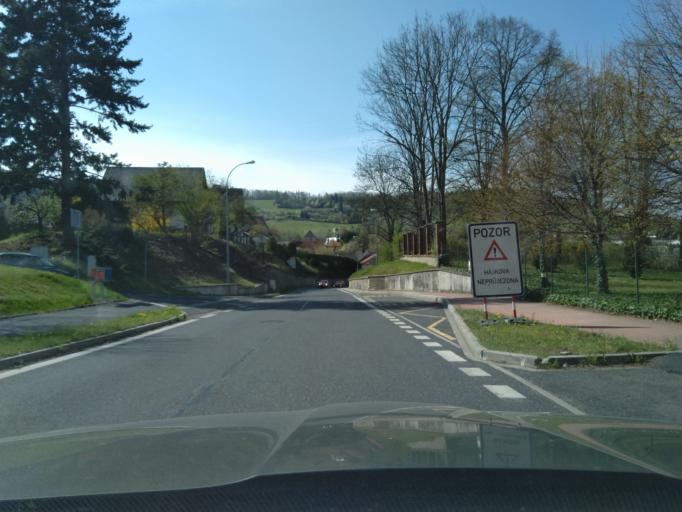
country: CZ
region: Plzensky
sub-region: Okres Klatovy
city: Susice
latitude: 49.2300
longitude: 13.5270
